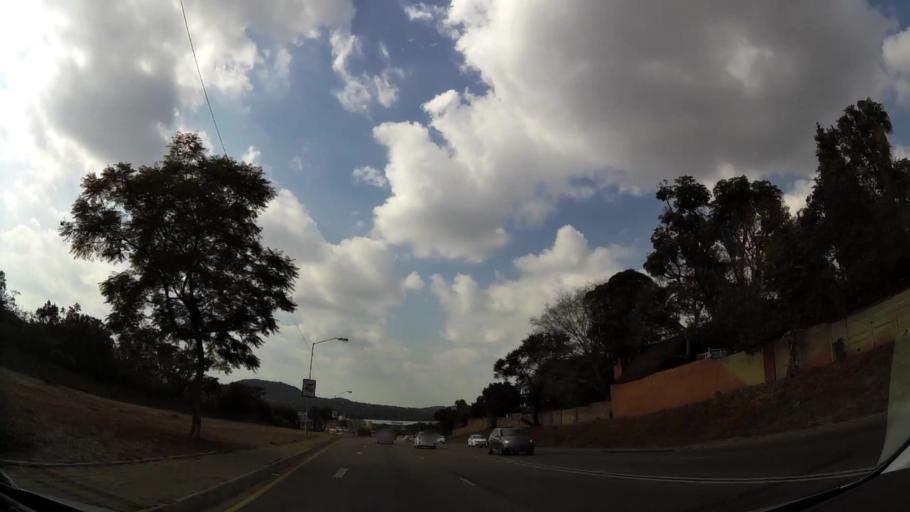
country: ZA
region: Gauteng
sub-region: City of Tshwane Metropolitan Municipality
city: Pretoria
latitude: -25.7836
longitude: 28.2971
